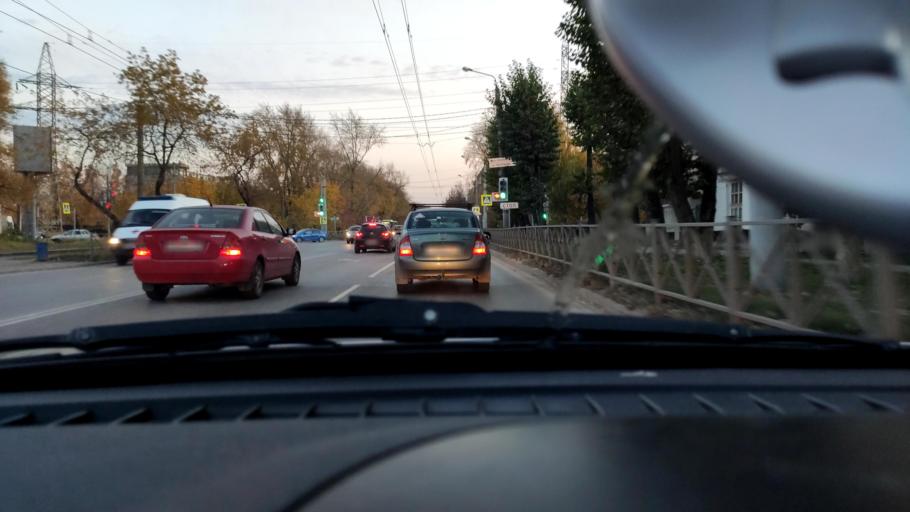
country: RU
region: Perm
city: Perm
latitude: 57.9692
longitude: 56.2454
